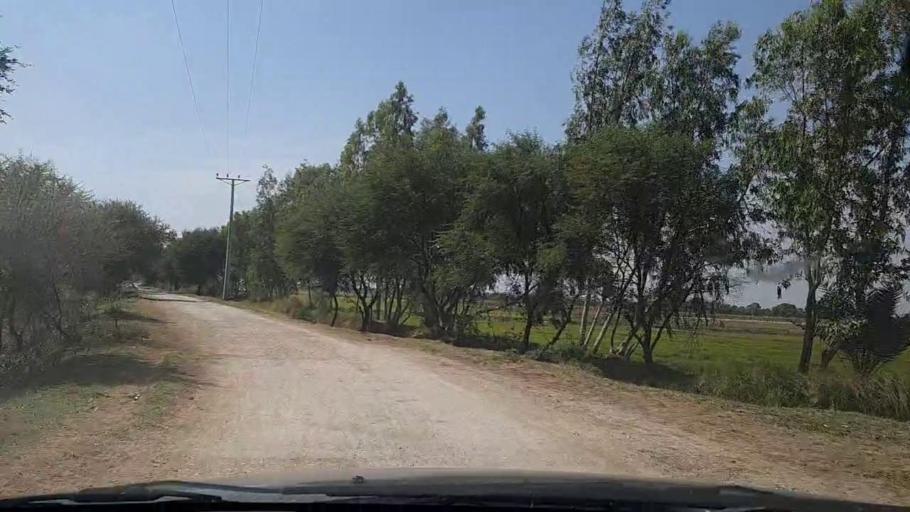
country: PK
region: Sindh
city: Mirpur Batoro
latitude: 24.6106
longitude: 68.2389
